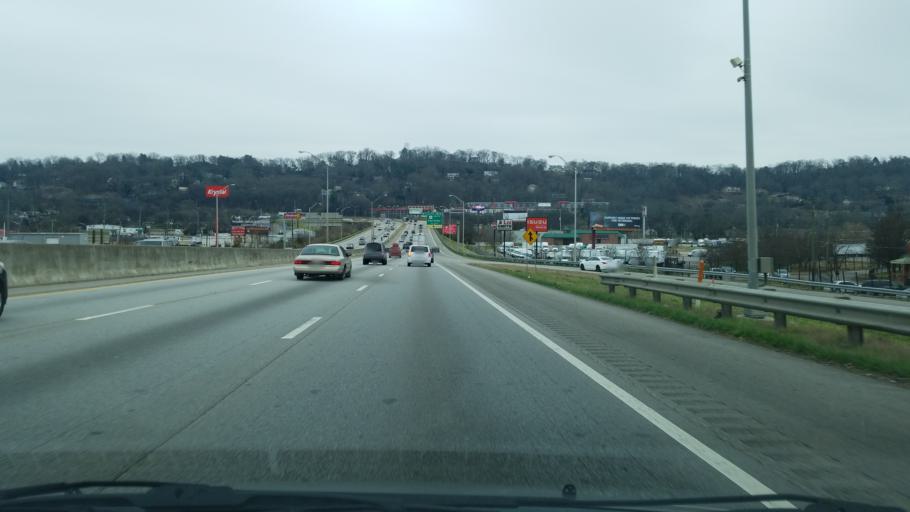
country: US
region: Tennessee
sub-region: Hamilton County
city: East Ridge
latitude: 35.0163
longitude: -85.2801
